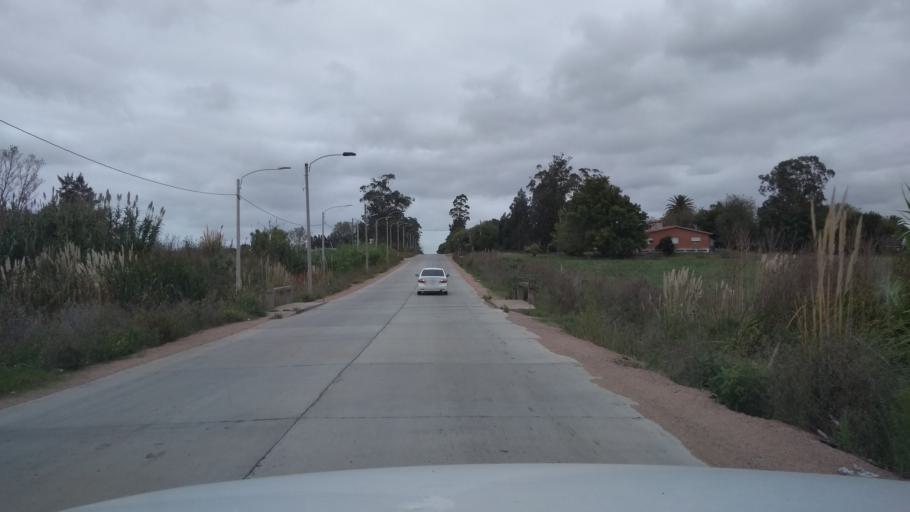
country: UY
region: Canelones
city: Toledo
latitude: -34.7924
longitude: -56.1478
